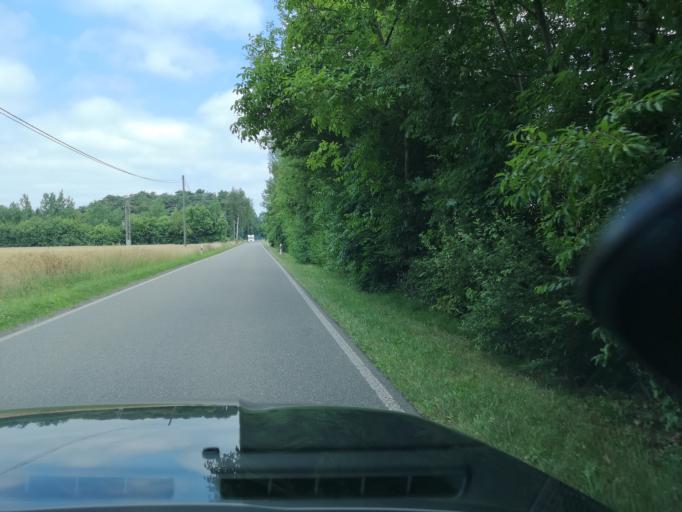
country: DE
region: North Rhine-Westphalia
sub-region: Regierungsbezirk Munster
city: Rhede
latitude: 51.8739
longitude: 6.6884
